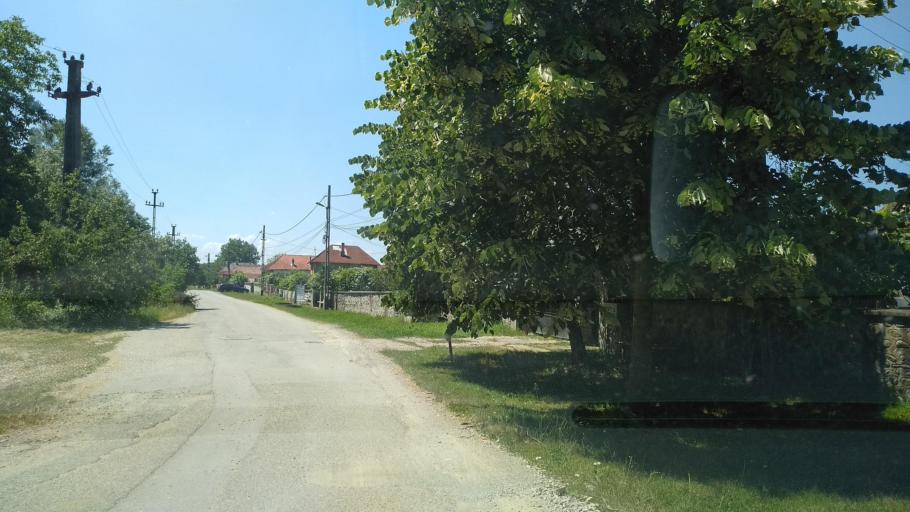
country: RO
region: Gorj
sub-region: Comuna Turcinesti
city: Turcinesti
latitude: 45.1171
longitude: 23.3156
